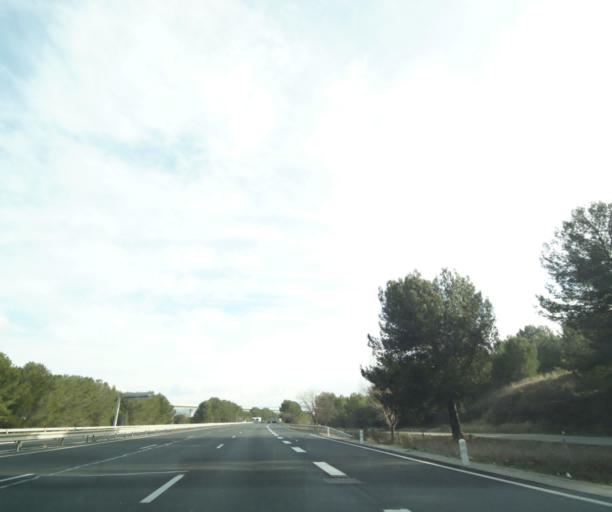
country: FR
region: Provence-Alpes-Cote d'Azur
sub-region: Departement des Bouches-du-Rhone
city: Ventabren
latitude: 43.5500
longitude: 5.3225
